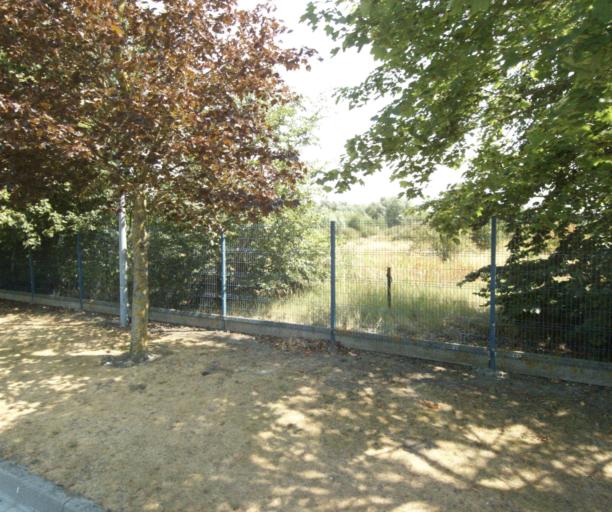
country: FR
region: Nord-Pas-de-Calais
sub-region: Departement du Nord
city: Comines
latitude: 50.7711
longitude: 3.0179
